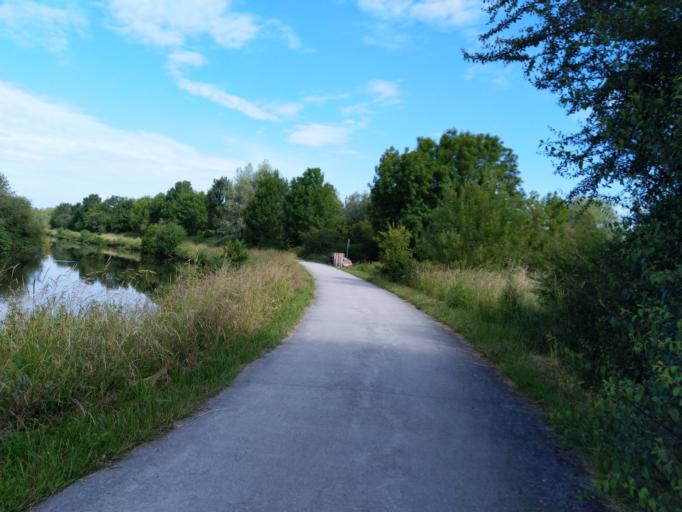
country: FR
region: Nord-Pas-de-Calais
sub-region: Departement du Nord
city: Boussois
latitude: 50.2852
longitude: 4.0533
